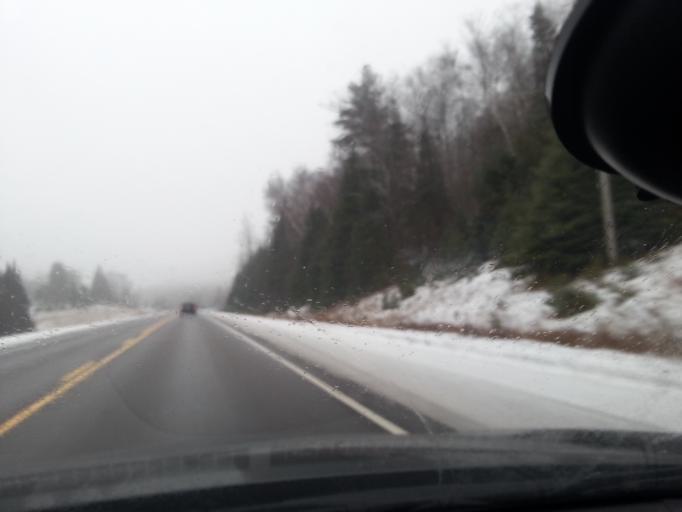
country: CA
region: Ontario
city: Skatepark
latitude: 44.7551
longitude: -76.8190
